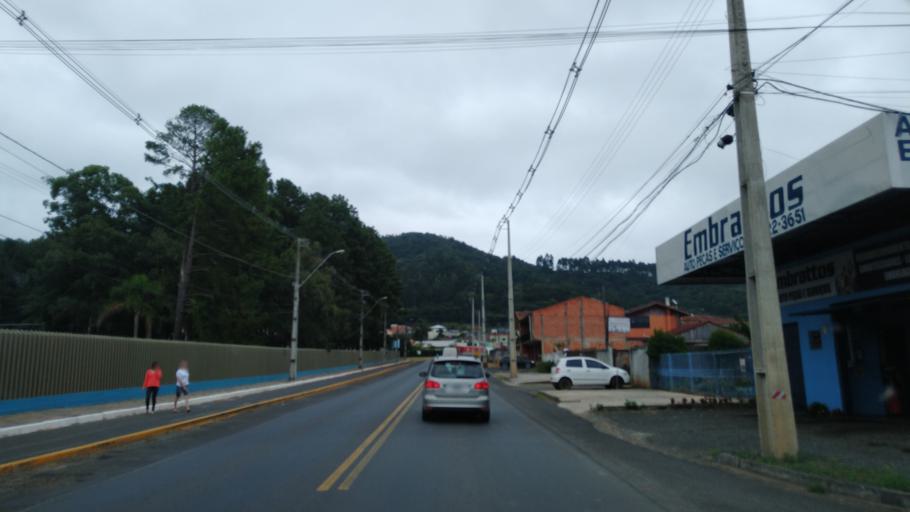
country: BR
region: Santa Catarina
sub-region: Porto Uniao
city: Porto Uniao
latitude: -26.2578
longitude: -51.0707
